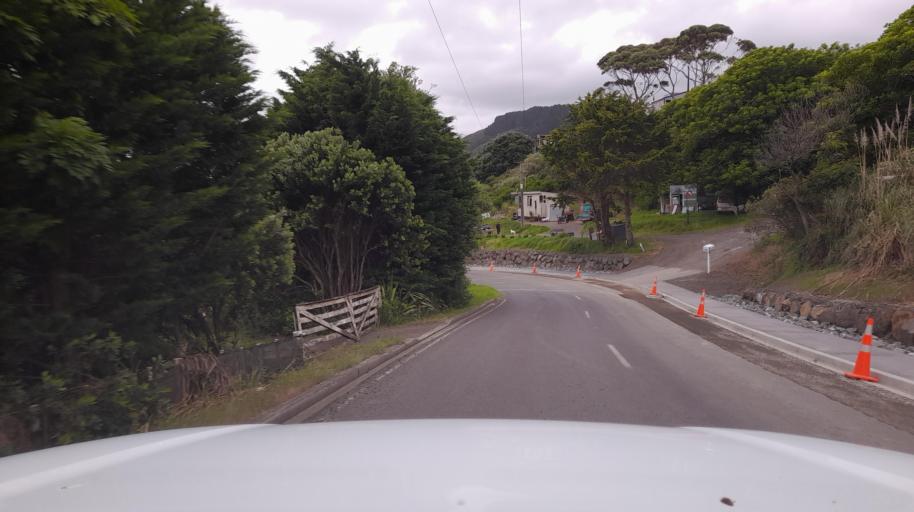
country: NZ
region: Northland
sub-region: Far North District
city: Ahipara
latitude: -35.1795
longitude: 173.1295
